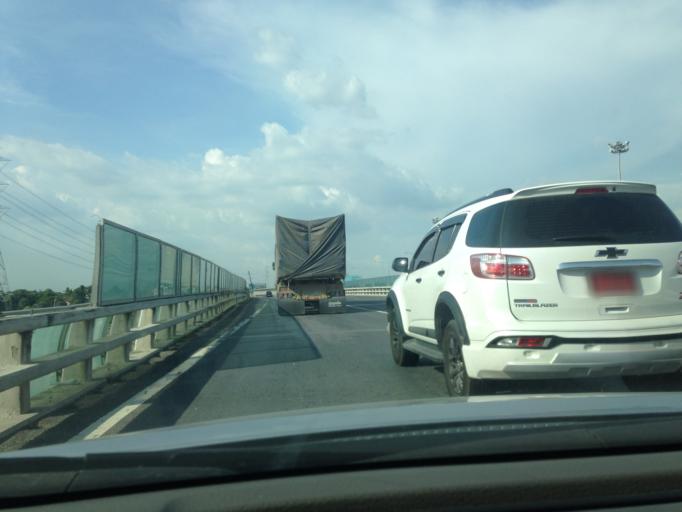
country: TH
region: Bangkok
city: Saphan Sung
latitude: 13.7317
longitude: 100.7023
